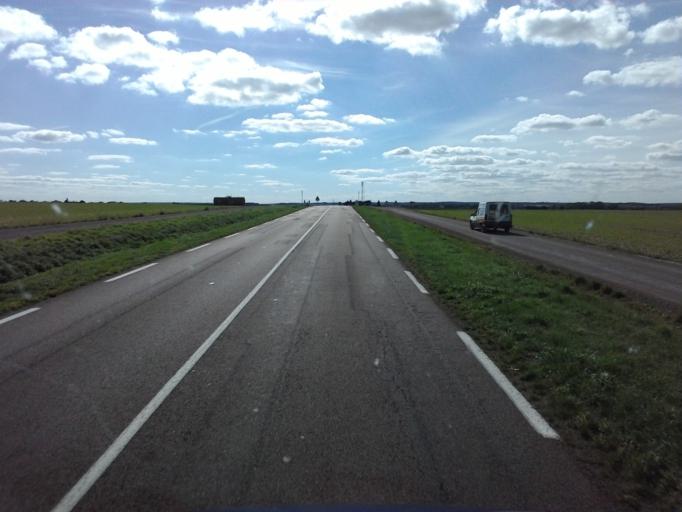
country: FR
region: Bourgogne
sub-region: Departement de la Cote-d'Or
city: Chatillon-sur-Seine
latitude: 47.8791
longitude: 4.5899
